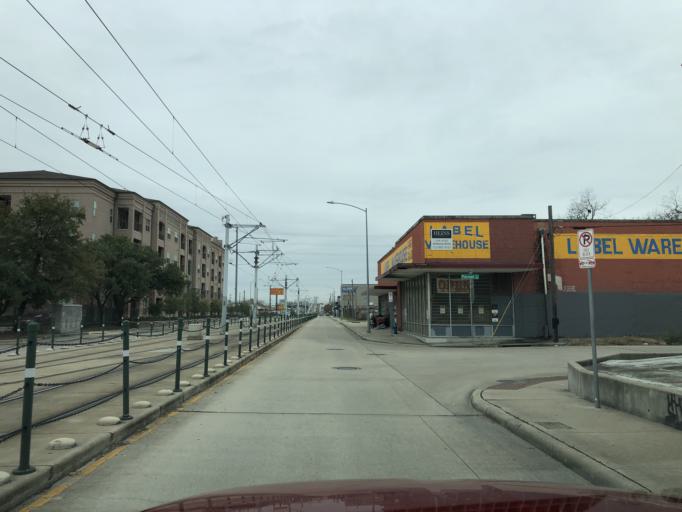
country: US
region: Texas
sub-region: Harris County
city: Houston
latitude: 29.7787
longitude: -95.3629
